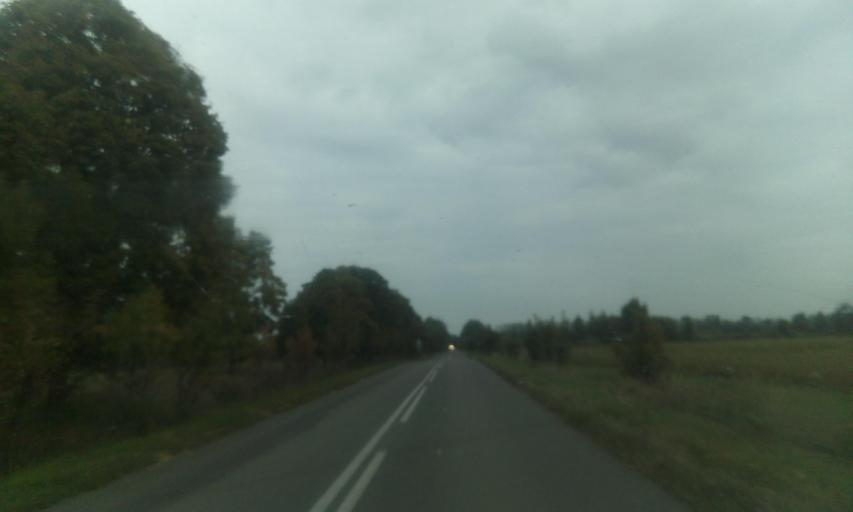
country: RU
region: Tula
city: Dubovka
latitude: 53.9576
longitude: 38.0736
